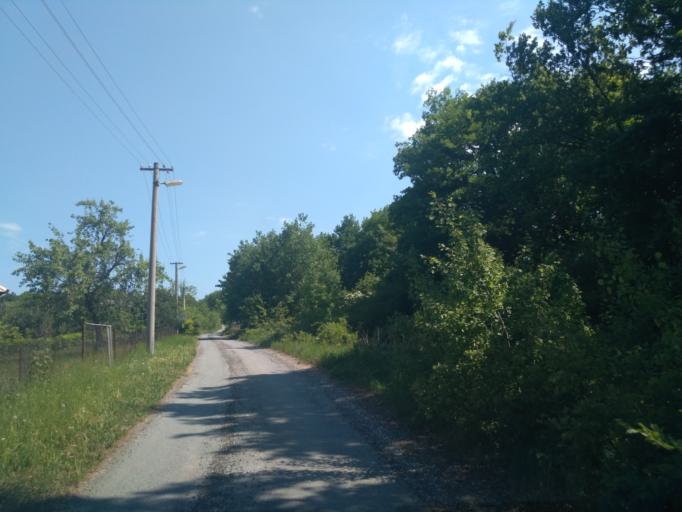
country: SK
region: Kosicky
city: Kosice
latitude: 48.8472
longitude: 21.4392
